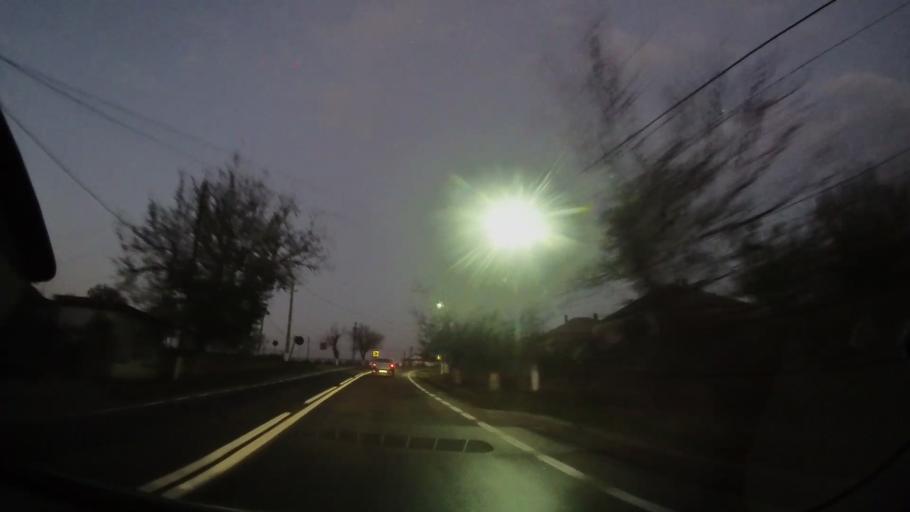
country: RO
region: Tulcea
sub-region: Comuna Frecatei
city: Cataloi
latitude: 45.1006
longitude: 28.7296
